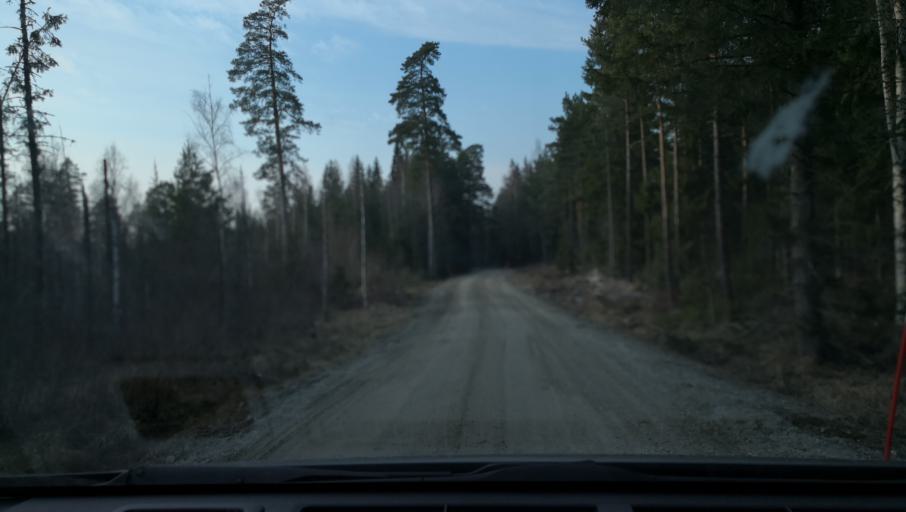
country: SE
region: OErebro
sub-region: Orebro Kommun
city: Hovsta
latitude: 59.3721
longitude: 15.3185
